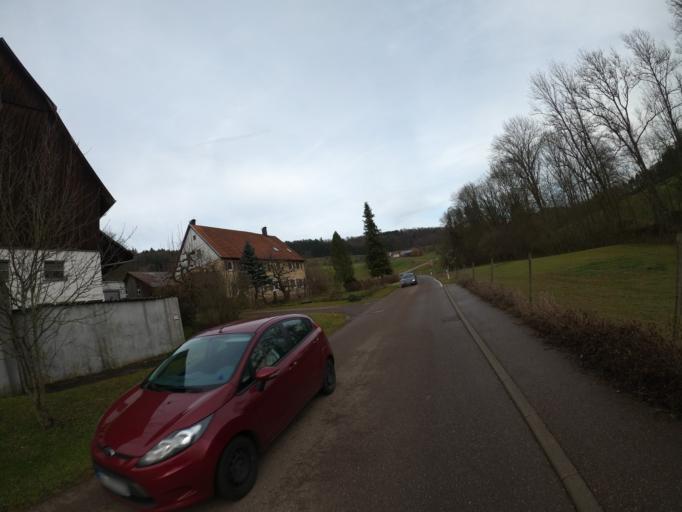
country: DE
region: Baden-Wuerttemberg
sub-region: Regierungsbezirk Stuttgart
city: Ottenbach
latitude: 48.7463
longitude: 9.7544
